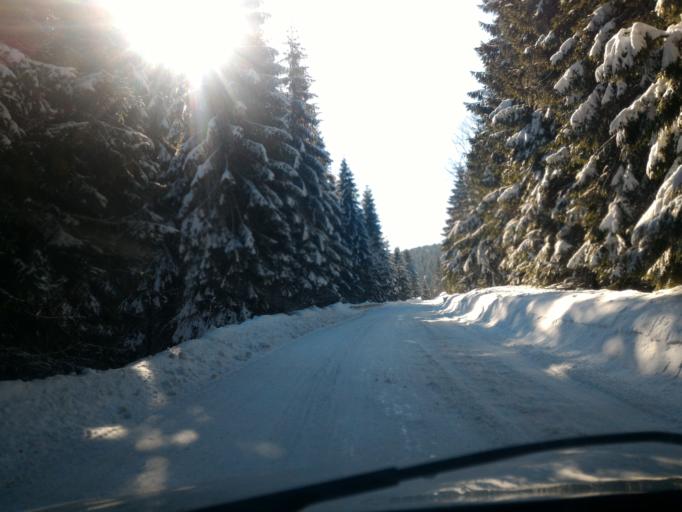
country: CZ
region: Liberecky
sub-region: Okres Jablonec nad Nisou
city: Josefuv Dul
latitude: 50.8481
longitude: 15.2684
